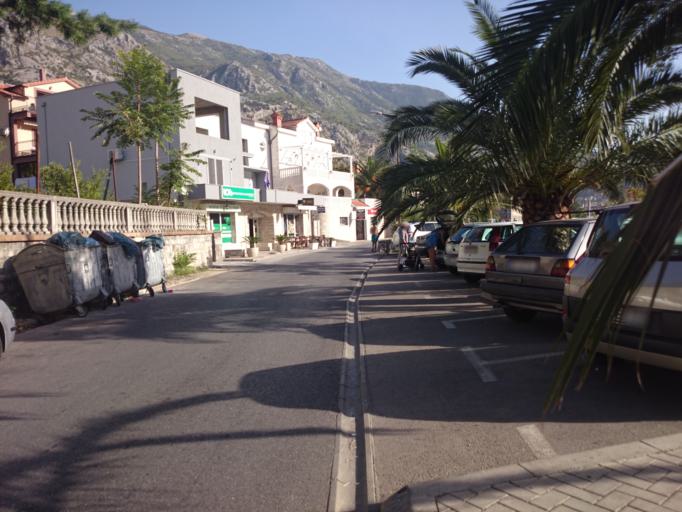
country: ME
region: Kotor
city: Kotor
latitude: 42.4314
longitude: 18.7674
